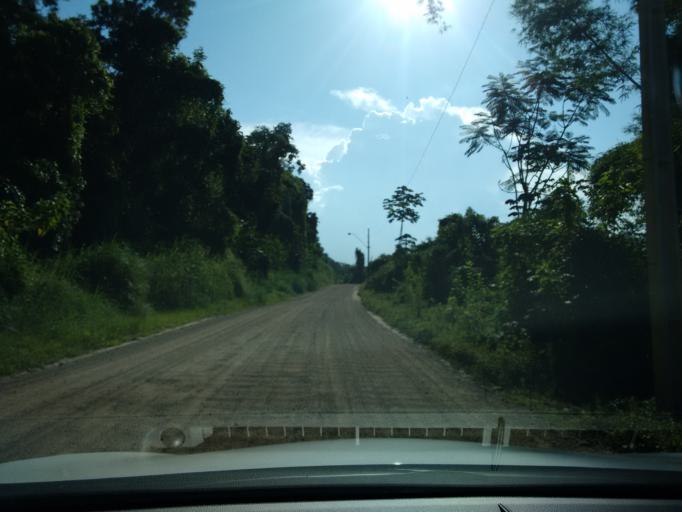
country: BR
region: Santa Catarina
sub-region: Blumenau
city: Blumenau
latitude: -26.8979
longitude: -49.0688
